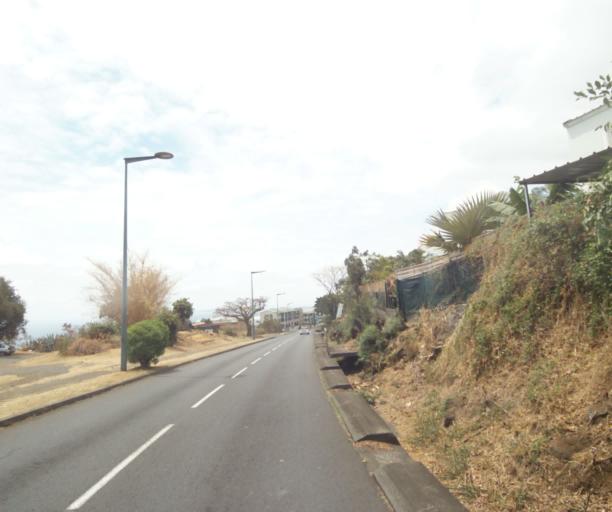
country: RE
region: Reunion
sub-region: Reunion
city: Saint-Paul
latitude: -21.0276
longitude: 55.2652
